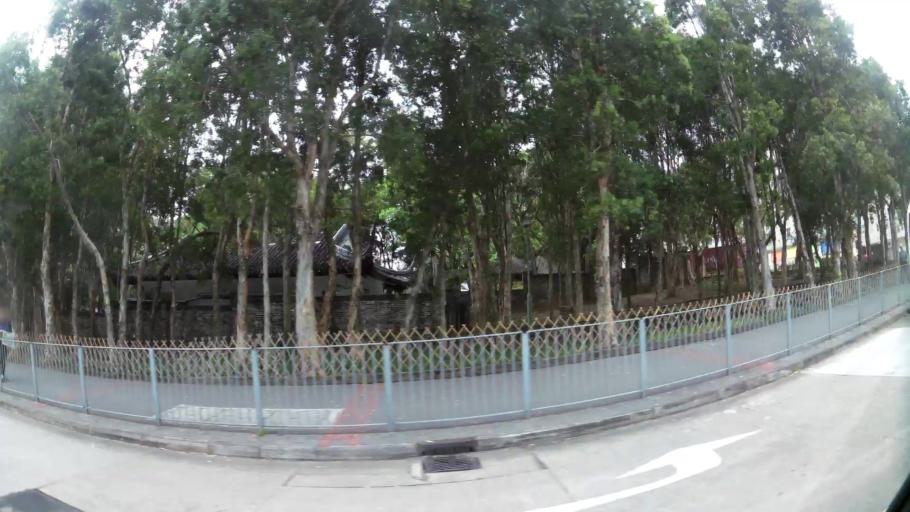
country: HK
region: Kowloon City
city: Kowloon
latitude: 22.3331
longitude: 114.1910
